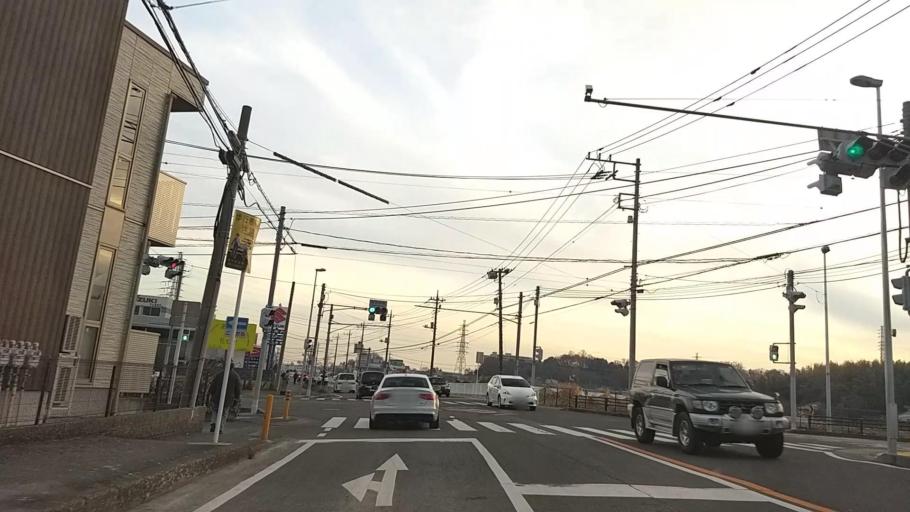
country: JP
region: Kanagawa
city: Atsugi
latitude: 35.4360
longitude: 139.3520
